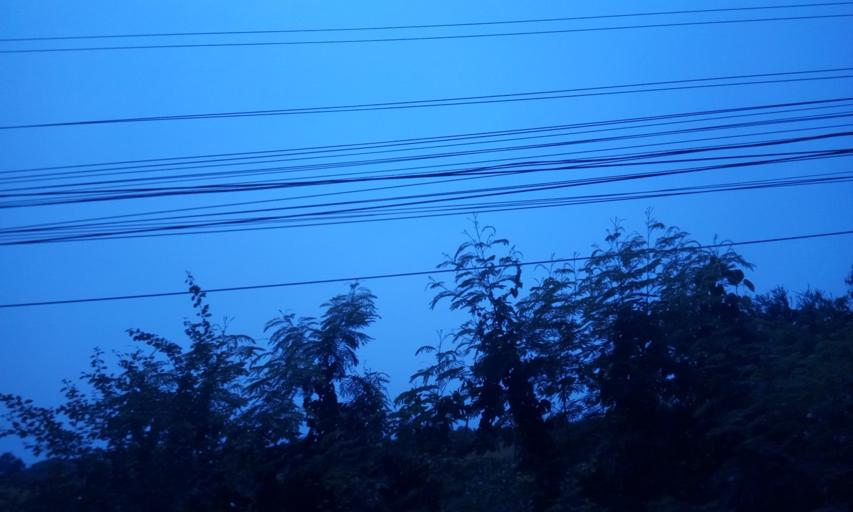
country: TH
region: Nonthaburi
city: Sai Noi
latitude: 13.9479
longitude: 100.3137
